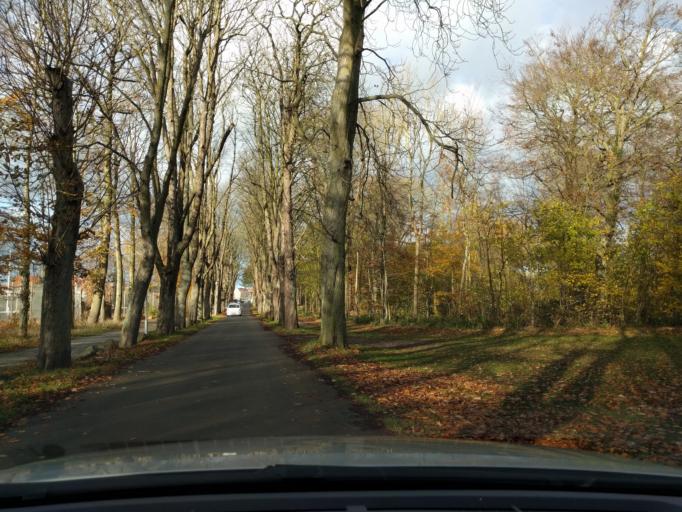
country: DK
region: South Denmark
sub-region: Kerteminde Kommune
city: Kerteminde
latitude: 55.4442
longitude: 10.6632
